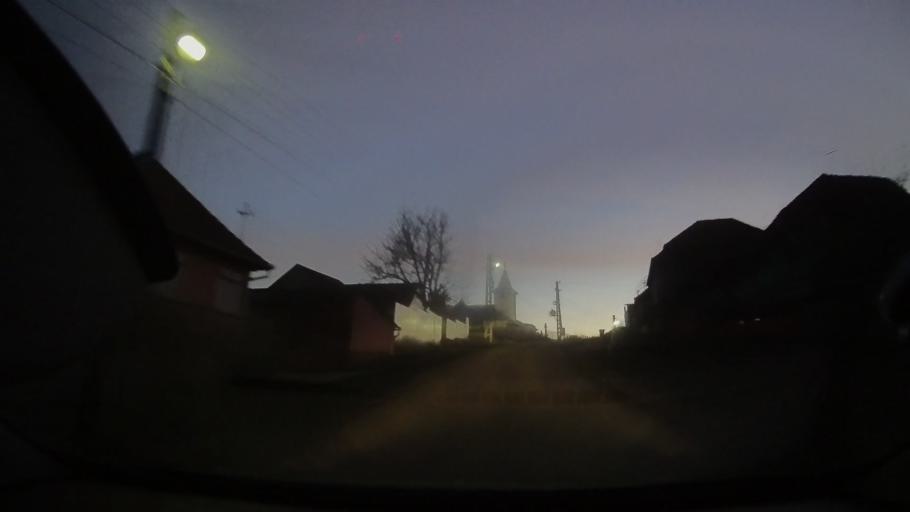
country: RO
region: Bihor
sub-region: Comuna Varciorog
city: Varciorog
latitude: 46.9757
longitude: 22.3258
